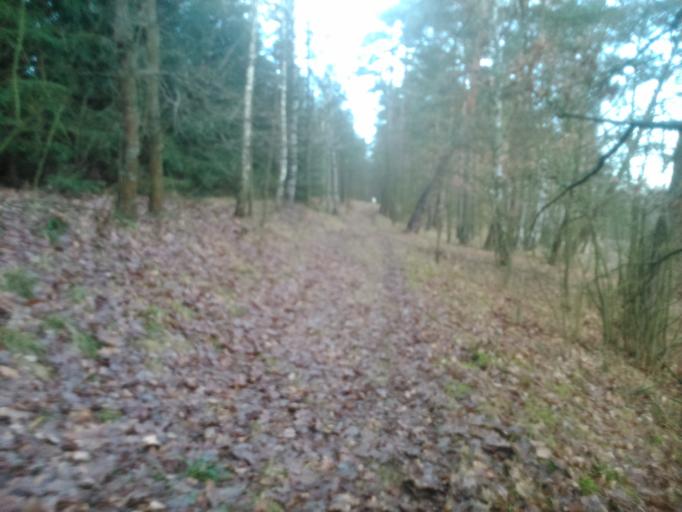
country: PL
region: Kujawsko-Pomorskie
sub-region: Powiat golubsko-dobrzynski
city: Golub-Dobrzyn
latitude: 53.1343
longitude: 19.1284
